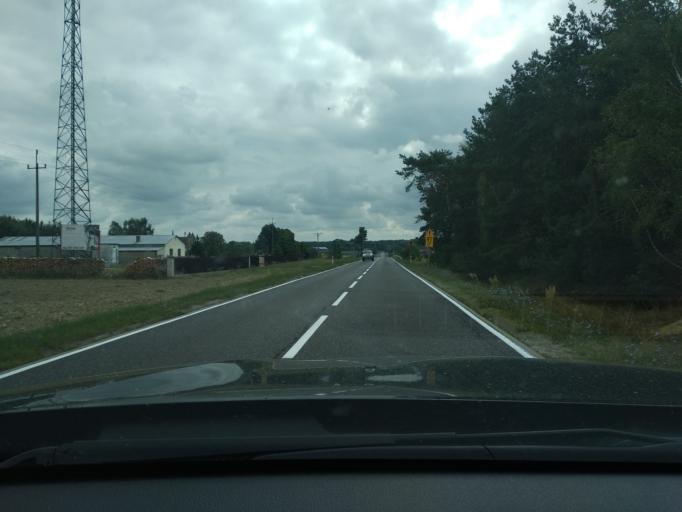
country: PL
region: Masovian Voivodeship
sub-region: Powiat pultuski
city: Obryte
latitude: 52.6515
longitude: 21.2405
